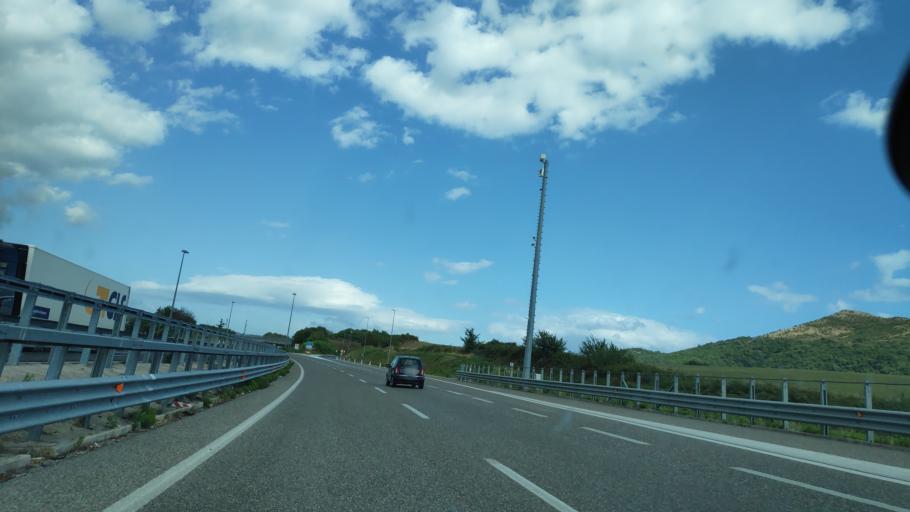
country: IT
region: Campania
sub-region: Provincia di Salerno
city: Palomonte
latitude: 40.6103
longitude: 15.2876
